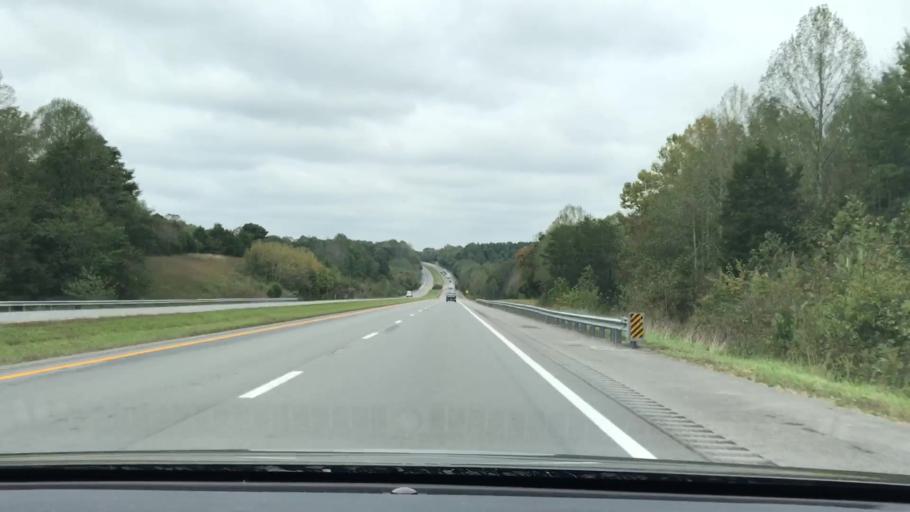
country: US
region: Kentucky
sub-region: Russell County
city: Russell Springs
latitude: 37.0568
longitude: -85.1707
